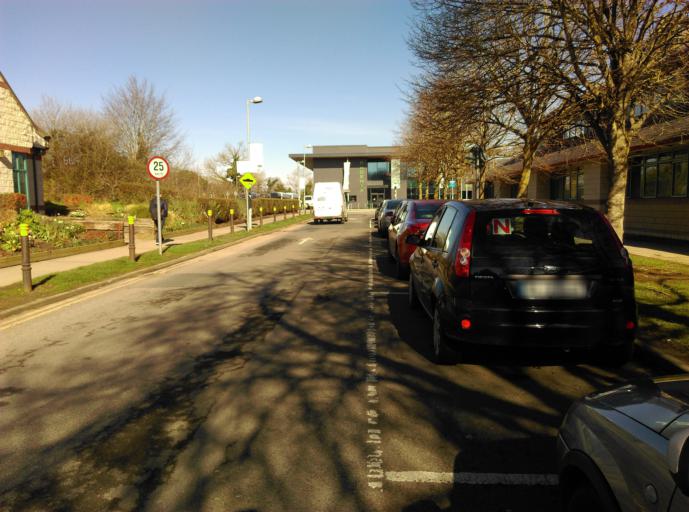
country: IE
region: Leinster
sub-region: Kildare
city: Maynooth
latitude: 53.3832
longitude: -6.6032
